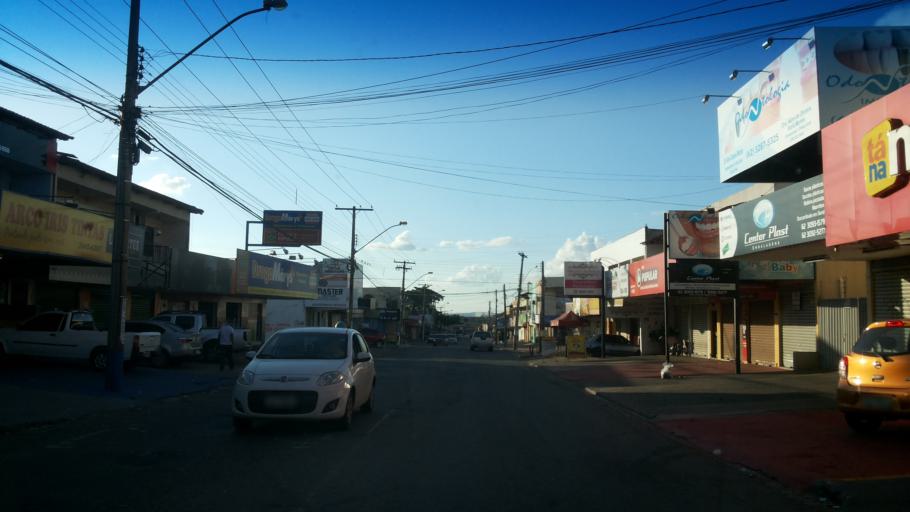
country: BR
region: Goias
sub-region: Goiania
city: Goiania
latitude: -16.7237
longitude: -49.3047
